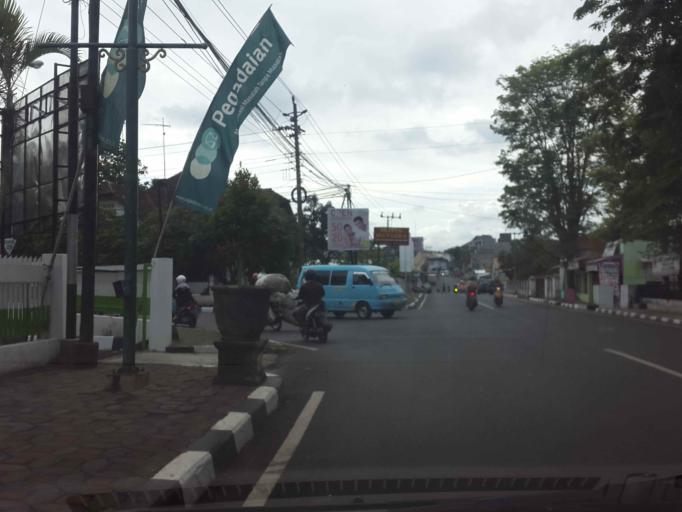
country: ID
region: Central Java
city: Salatiga
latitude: -7.3266
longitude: 110.5011
